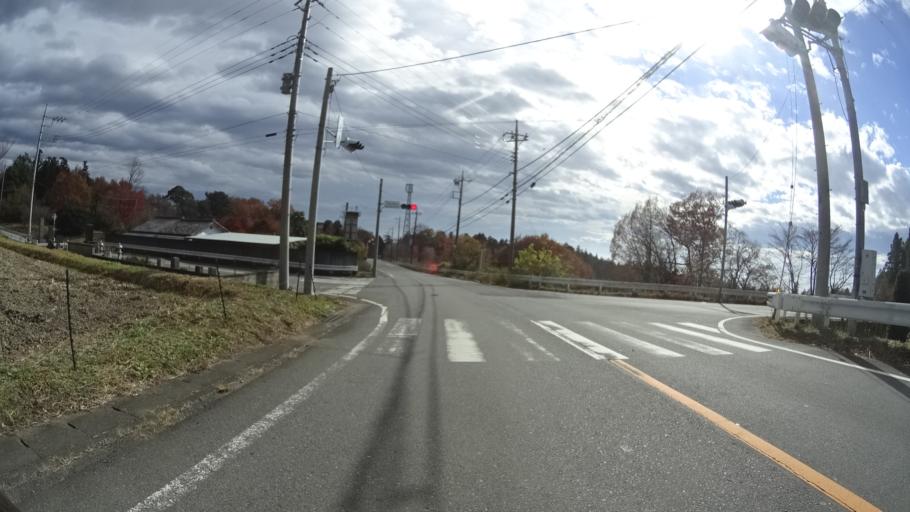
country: JP
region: Gunma
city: Omamacho-omama
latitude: 36.4803
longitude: 139.1766
